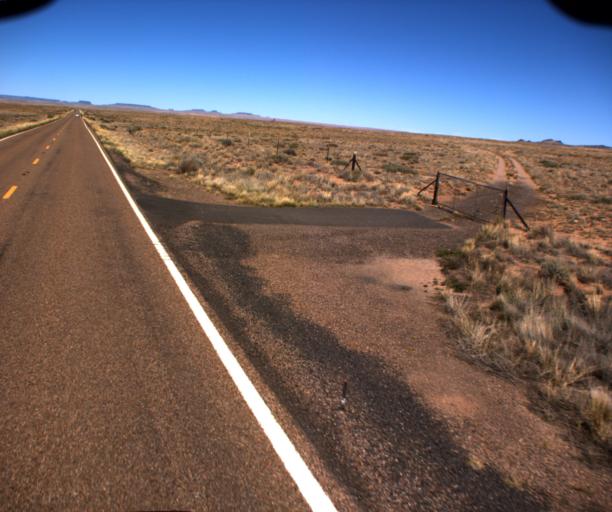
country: US
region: Arizona
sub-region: Navajo County
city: Holbrook
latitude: 35.0160
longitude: -110.0901
